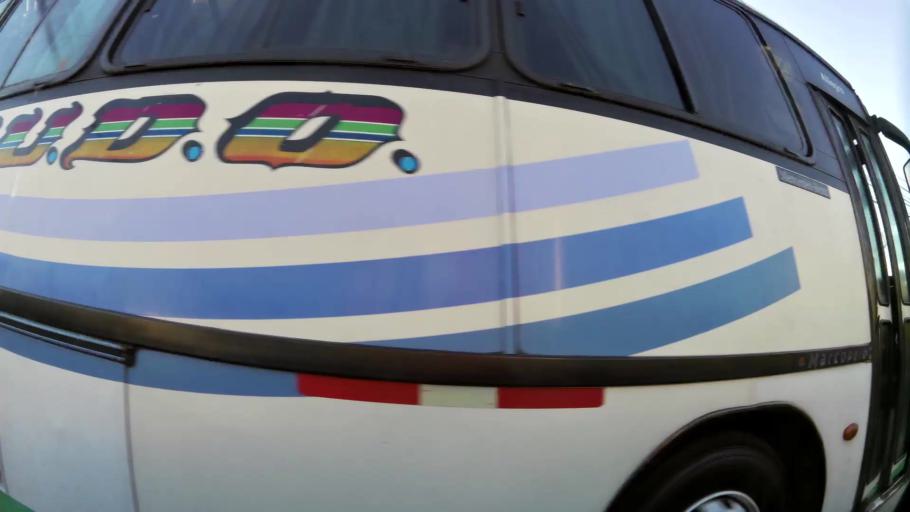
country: SV
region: La Libertad
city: Antiguo Cuscatlan
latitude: 13.6861
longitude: -89.2375
